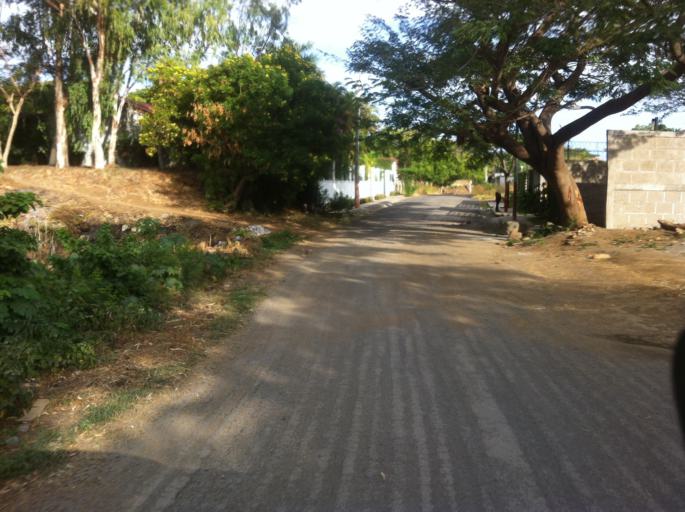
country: NI
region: Managua
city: Ciudad Sandino
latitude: 12.1004
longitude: -86.3254
